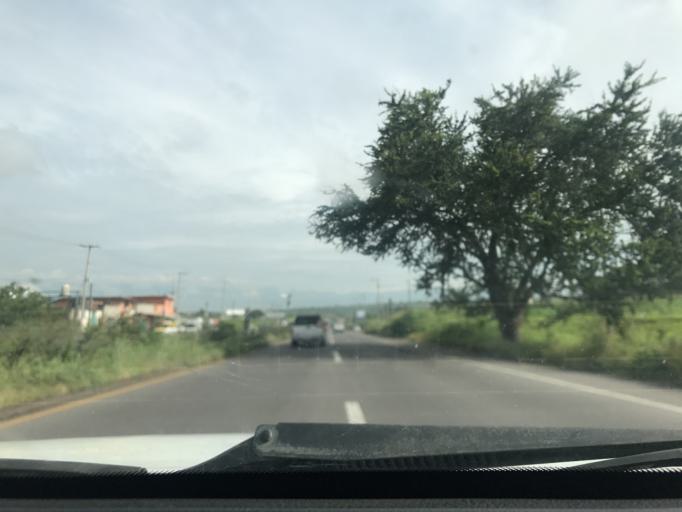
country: MX
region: Morelos
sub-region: Yecapixtla
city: Juan Morales
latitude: 18.8247
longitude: -98.9219
